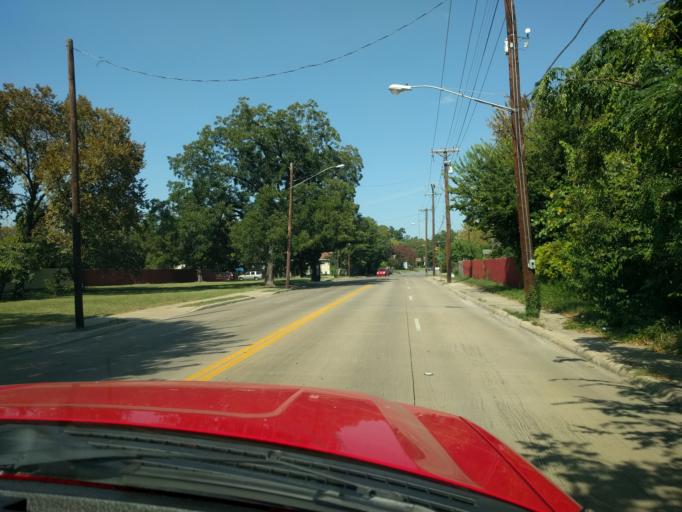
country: US
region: Texas
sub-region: Dallas County
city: Dallas
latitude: 32.7875
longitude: -96.7613
